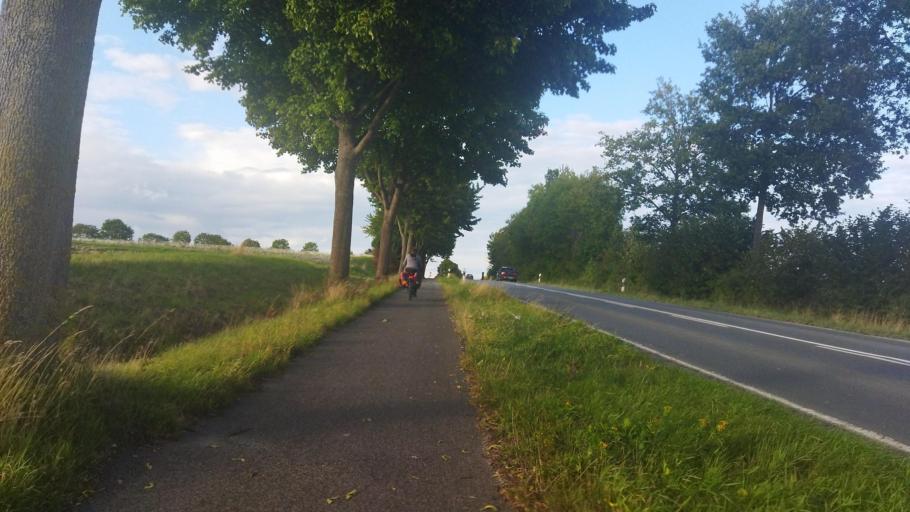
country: DE
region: North Rhine-Westphalia
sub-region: Regierungsbezirk Munster
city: Billerbeck
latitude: 51.9508
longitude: 7.2644
